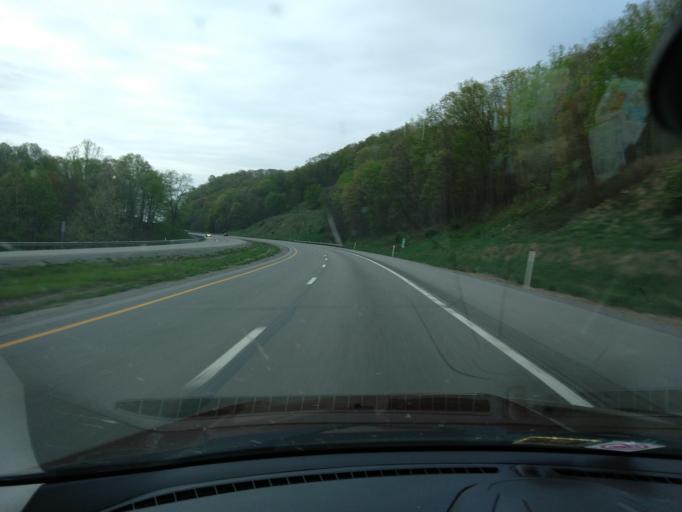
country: US
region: West Virginia
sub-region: Lewis County
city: Weston
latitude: 38.9216
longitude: -80.5506
